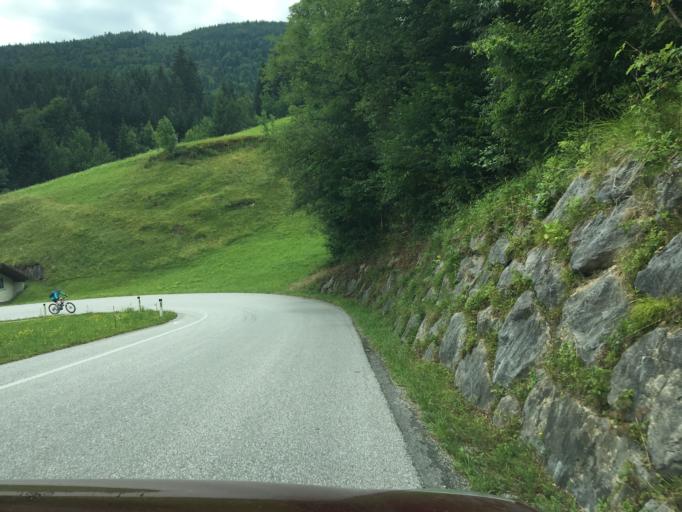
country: AT
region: Salzburg
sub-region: Politischer Bezirk Hallein
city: Abtenau
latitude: 47.5954
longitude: 13.3071
